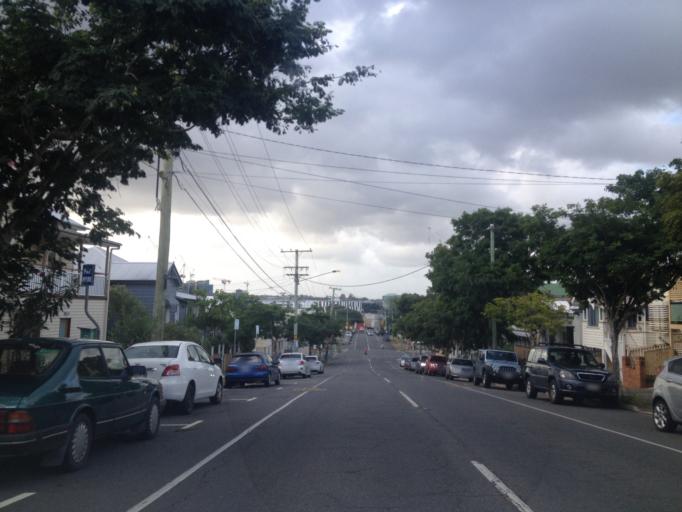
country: AU
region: Queensland
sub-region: Brisbane
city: Milton
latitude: -27.4816
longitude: 153.0071
